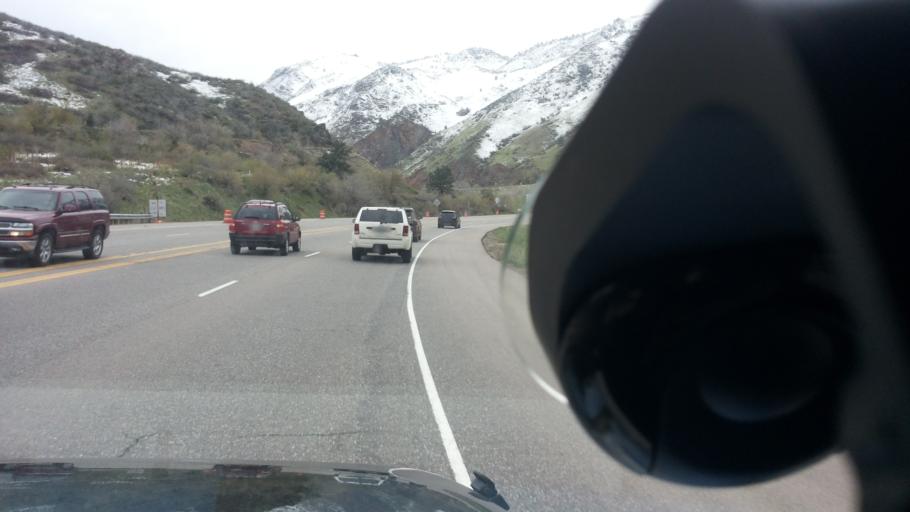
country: US
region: Colorado
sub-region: Jefferson County
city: Golden
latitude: 39.7508
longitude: -105.2321
